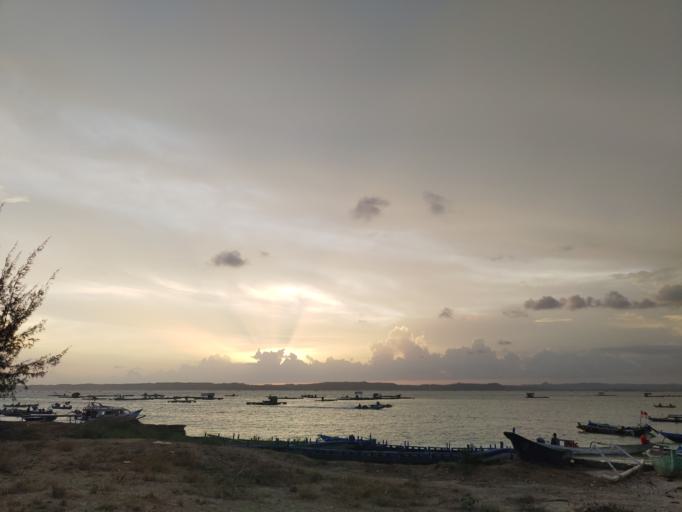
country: ID
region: West Nusa Tenggara
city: Pemongkong
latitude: -8.8743
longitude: 116.4546
